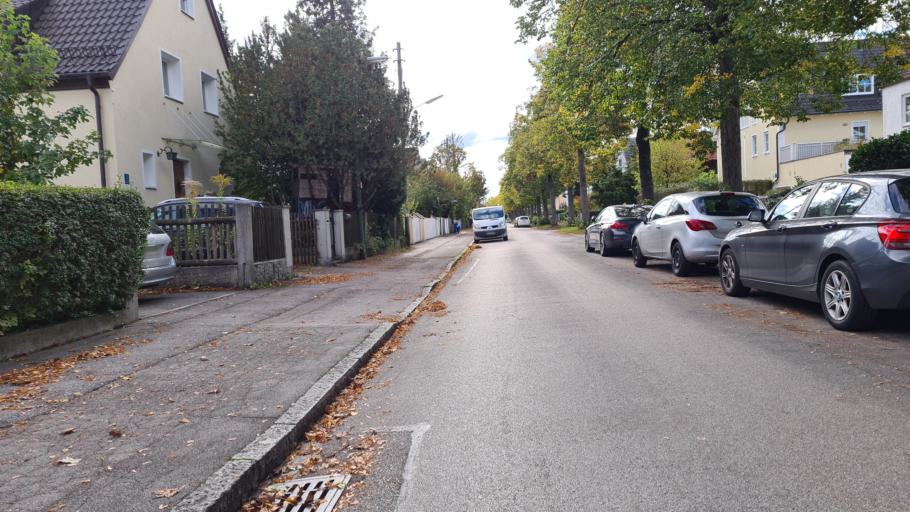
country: DE
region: Bavaria
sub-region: Upper Bavaria
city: Neuried
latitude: 48.1248
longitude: 11.5018
